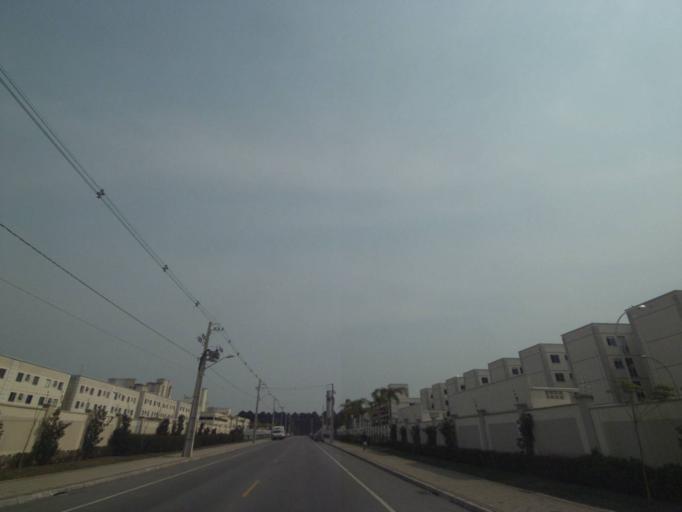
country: BR
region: Parana
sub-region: Sao Jose Dos Pinhais
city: Sao Jose dos Pinhais
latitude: -25.5165
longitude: -49.2832
